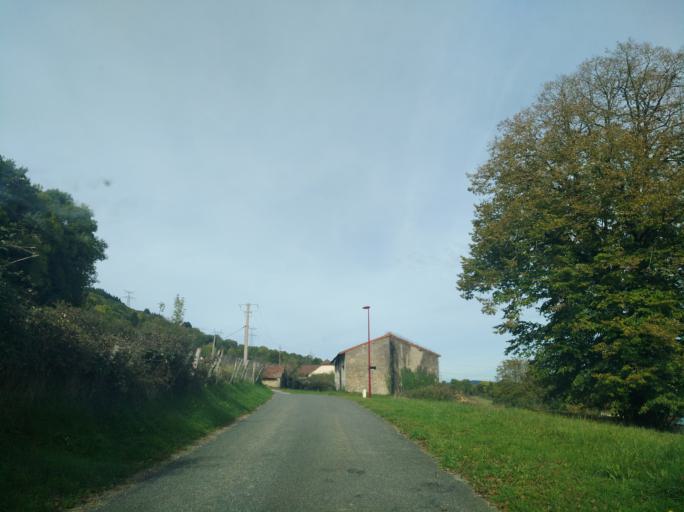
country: FR
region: Bourgogne
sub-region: Departement de Saone-et-Loire
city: Cuiseaux
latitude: 46.4514
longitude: 5.4218
